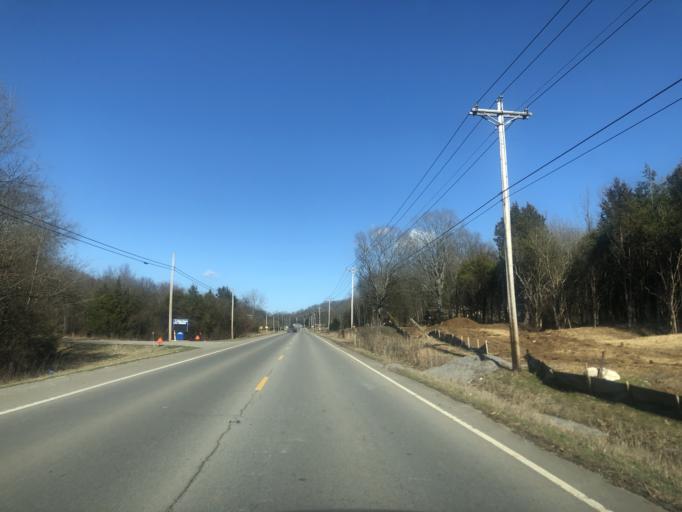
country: US
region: Tennessee
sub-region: Williamson County
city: Nolensville
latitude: 35.9135
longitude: -86.6606
